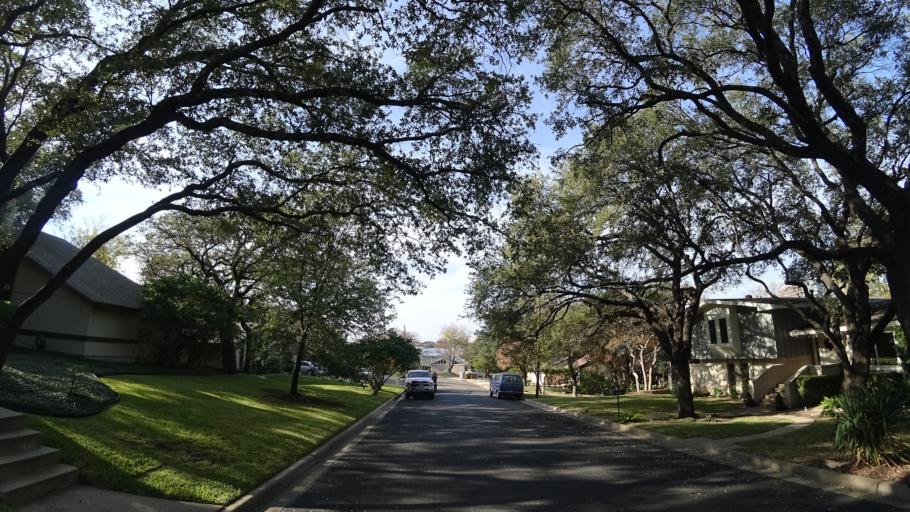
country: US
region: Texas
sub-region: Williamson County
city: Jollyville
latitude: 30.3864
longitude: -97.7512
